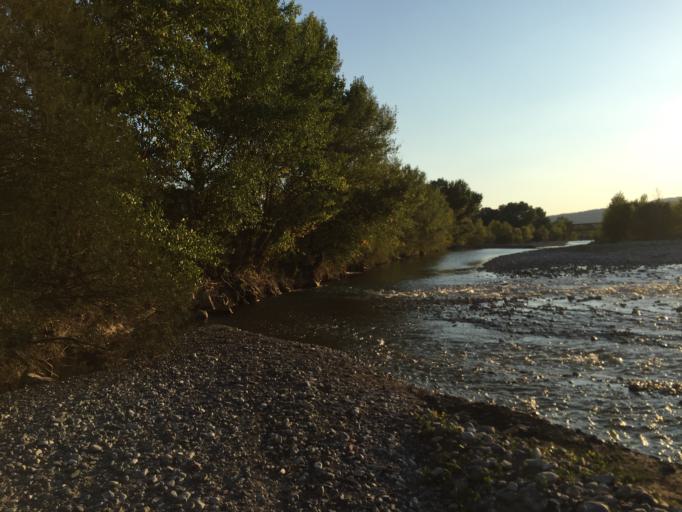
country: FR
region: Provence-Alpes-Cote d'Azur
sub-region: Departement des Alpes-de-Haute-Provence
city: Digne-les-Bains
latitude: 44.0788
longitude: 6.2098
